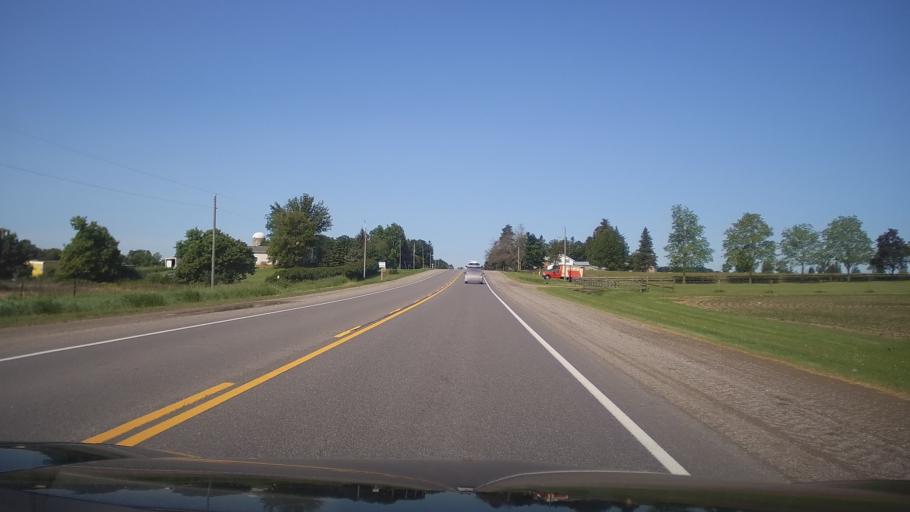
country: CA
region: Ontario
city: Omemee
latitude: 44.3421
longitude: -78.8389
